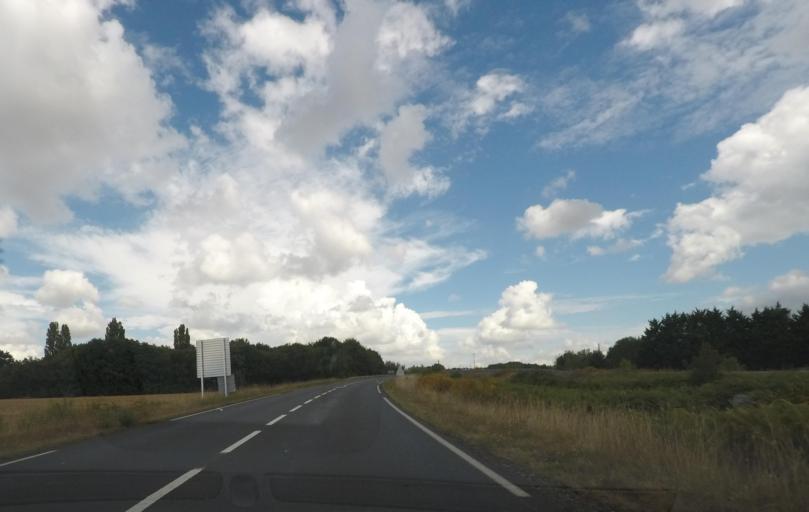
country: FR
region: Pays de la Loire
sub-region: Departement de la Sarthe
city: Champagne
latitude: 48.0454
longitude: 0.2924
